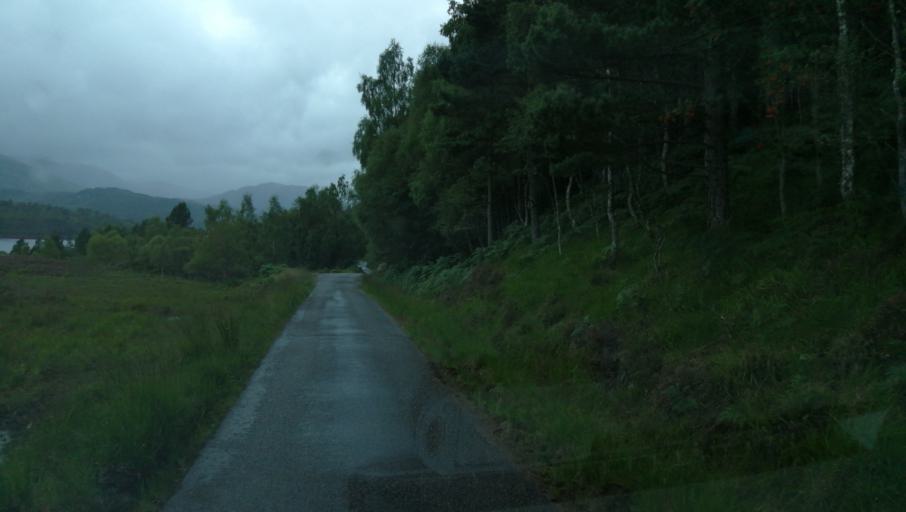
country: GB
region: Scotland
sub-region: Highland
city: Spean Bridge
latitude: 57.2789
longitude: -4.9400
